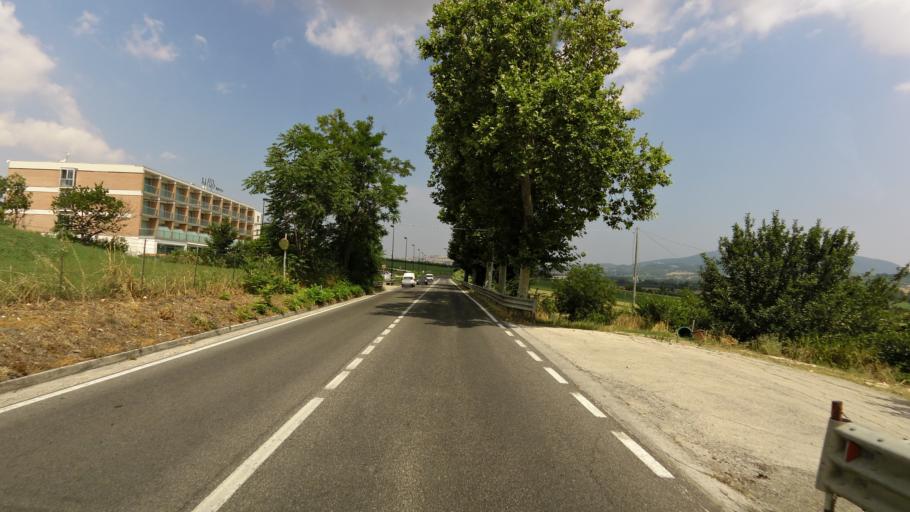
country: IT
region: The Marches
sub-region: Provincia di Ancona
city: Castelfidardo
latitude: 43.4797
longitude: 13.5793
